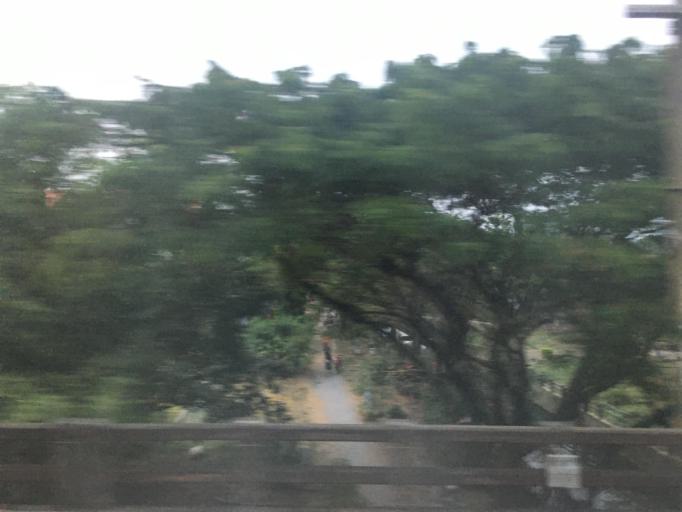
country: TW
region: Taiwan
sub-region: Pingtung
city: Pingtung
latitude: 22.6625
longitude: 120.4272
